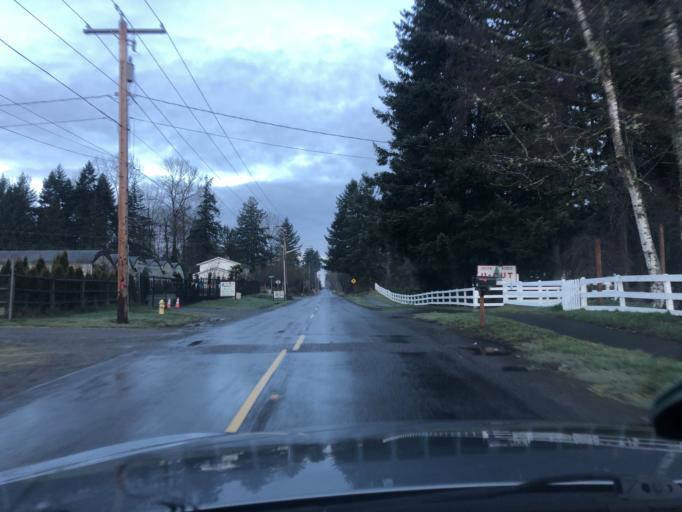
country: US
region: Washington
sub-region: Pierce County
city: North Puyallup
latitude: 47.2249
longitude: -122.2821
